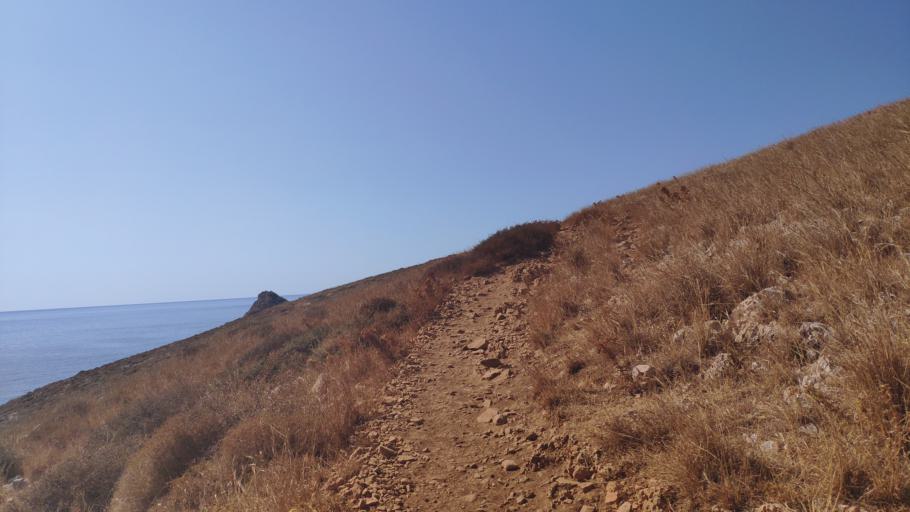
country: GR
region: Peloponnese
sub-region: Nomos Lakonias
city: Gytheio
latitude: 36.3980
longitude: 22.4849
